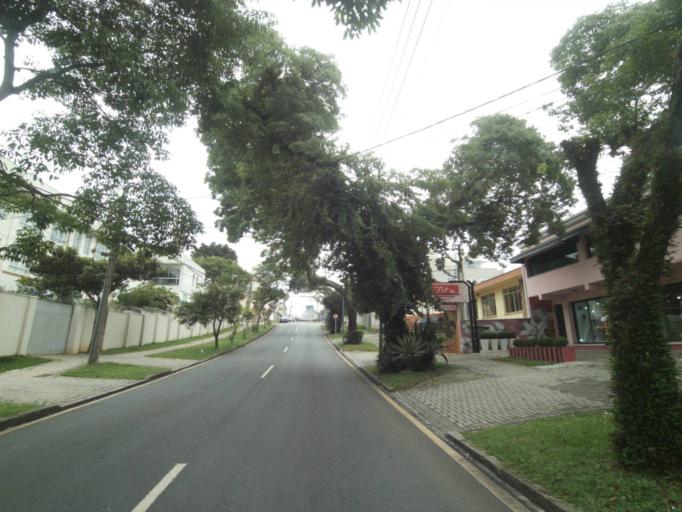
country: BR
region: Parana
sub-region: Curitiba
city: Curitiba
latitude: -25.4205
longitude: -49.2886
